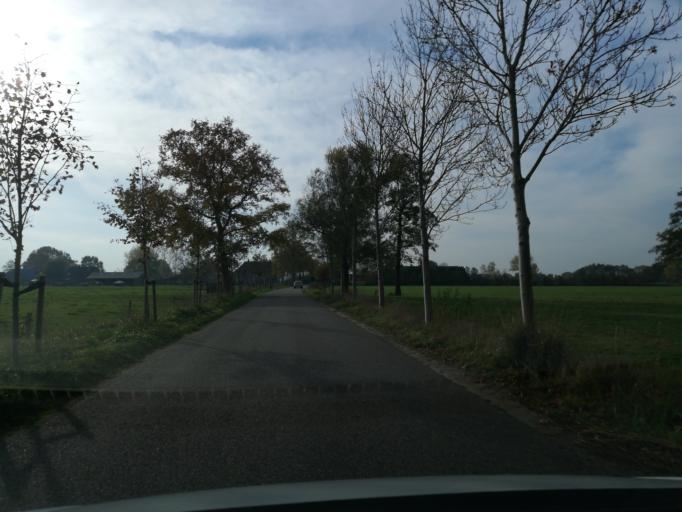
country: NL
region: Gelderland
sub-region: Gemeente Apeldoorn
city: Apeldoorn
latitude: 52.2466
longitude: 6.0305
